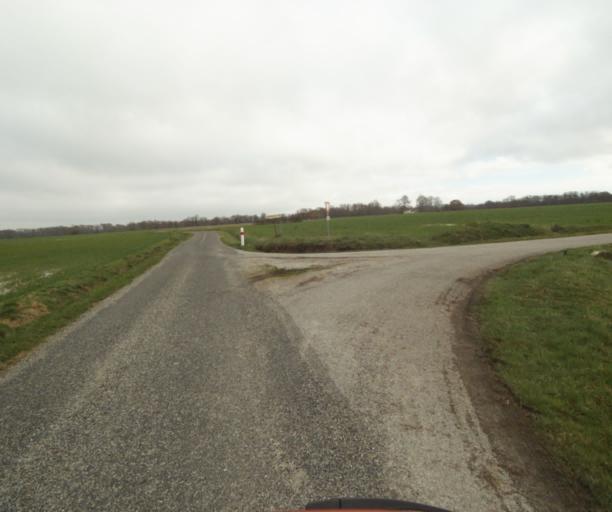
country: FR
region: Languedoc-Roussillon
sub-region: Departement de l'Aude
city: Belpech
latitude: 43.1801
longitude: 1.6941
